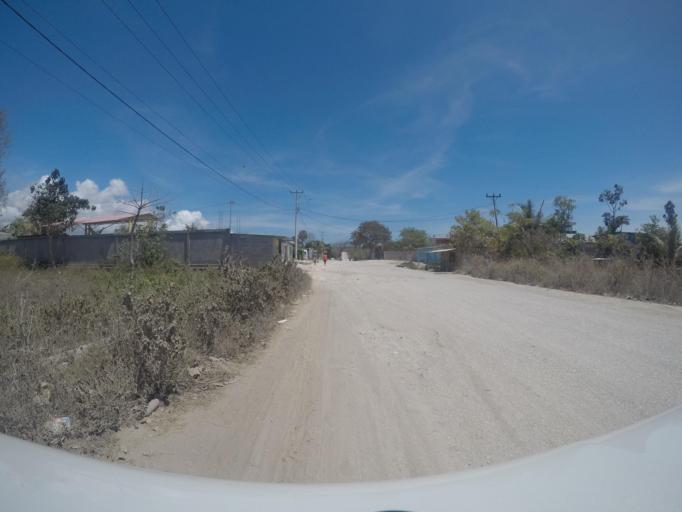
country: TL
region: Baucau
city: Baucau
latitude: -8.4753
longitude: 126.4478
